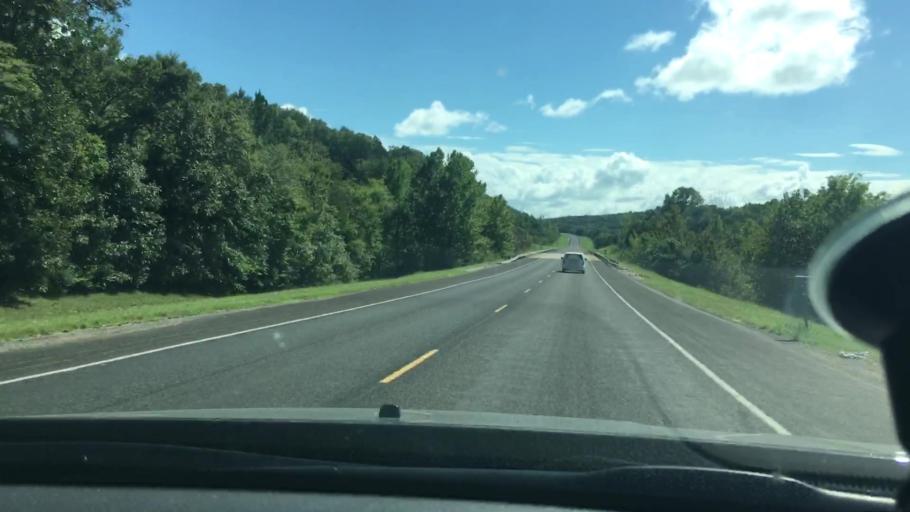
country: US
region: Oklahoma
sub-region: Sequoyah County
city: Vian
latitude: 35.5394
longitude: -94.9691
